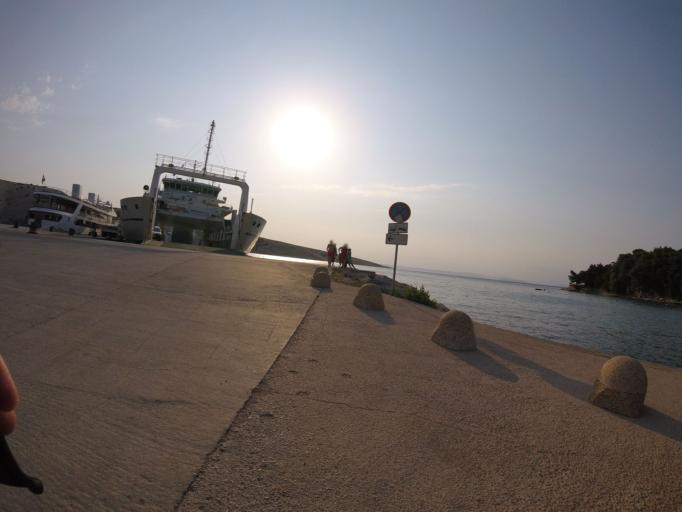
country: HR
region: Primorsko-Goranska
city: Lopar
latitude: 44.8379
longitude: 14.7217
